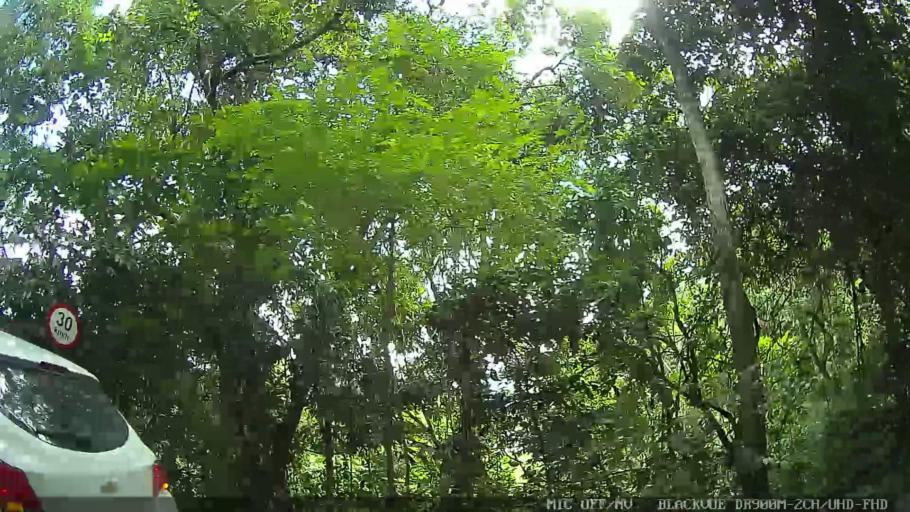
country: BR
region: Sao Paulo
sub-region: Caraguatatuba
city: Caraguatatuba
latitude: -23.6313
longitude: -45.4521
